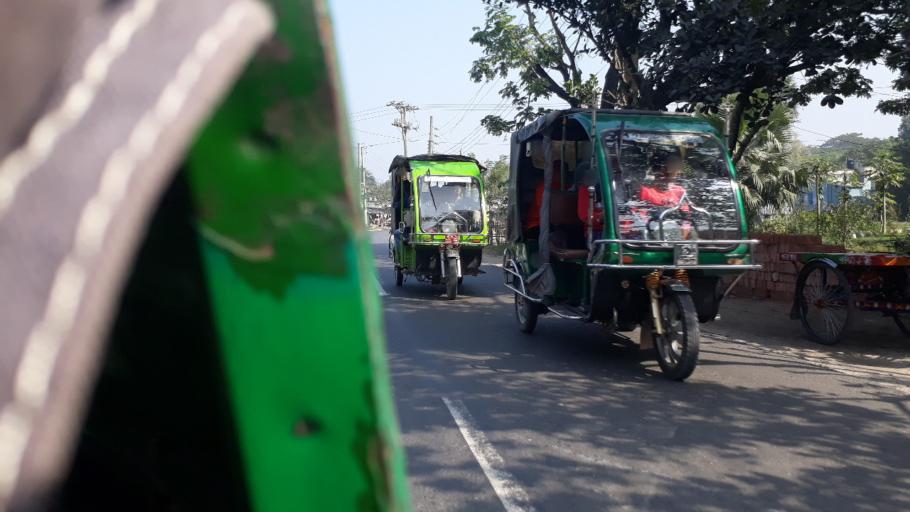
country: BD
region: Khulna
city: Kushtia
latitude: 23.8795
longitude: 89.0873
